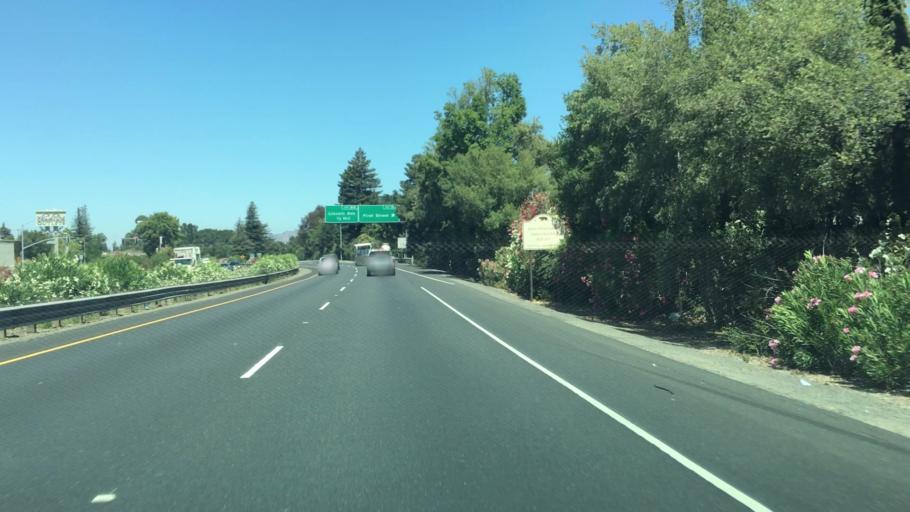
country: US
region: California
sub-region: Napa County
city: Napa
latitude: 38.2946
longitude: -122.3018
